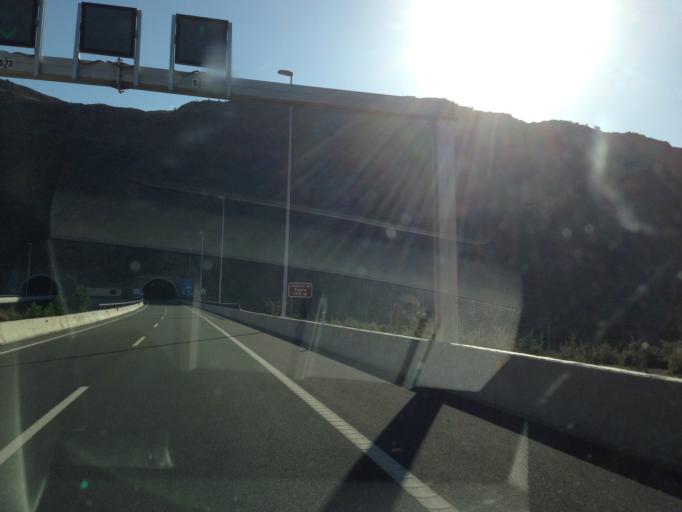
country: ES
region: Canary Islands
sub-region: Provincia de Las Palmas
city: Puerto Rico
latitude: 27.8095
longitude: -15.7259
